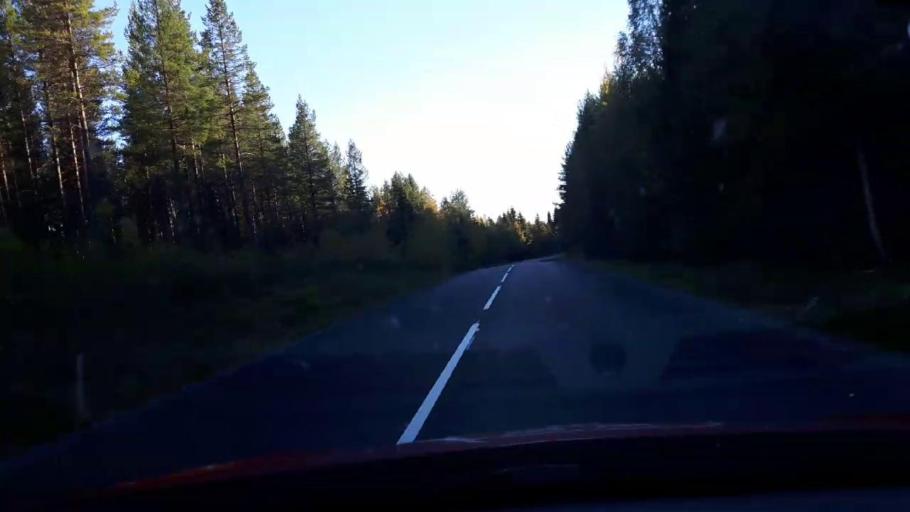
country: SE
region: Jaemtland
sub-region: OEstersunds Kommun
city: Lit
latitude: 63.4680
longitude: 14.8744
